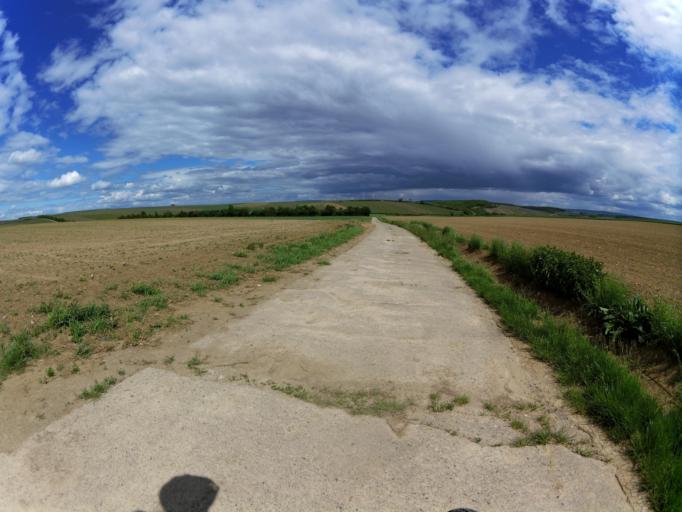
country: DE
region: Bavaria
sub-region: Regierungsbezirk Unterfranken
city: Volkach
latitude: 49.8826
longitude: 10.2330
